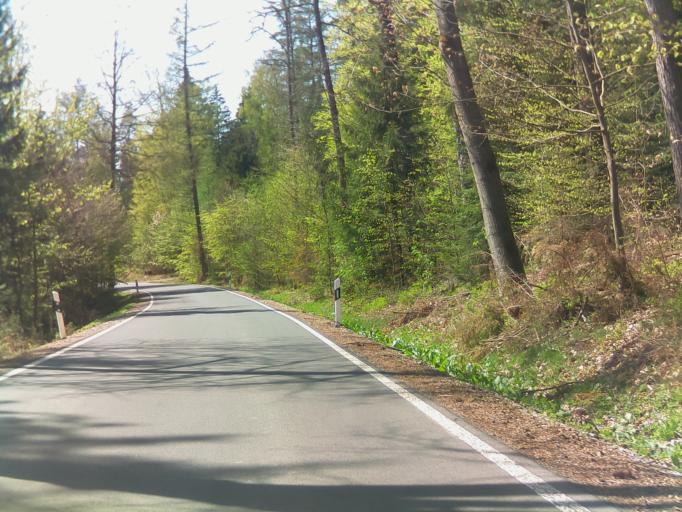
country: DE
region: Thuringia
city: Hildburghausen
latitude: 50.4471
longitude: 10.7656
